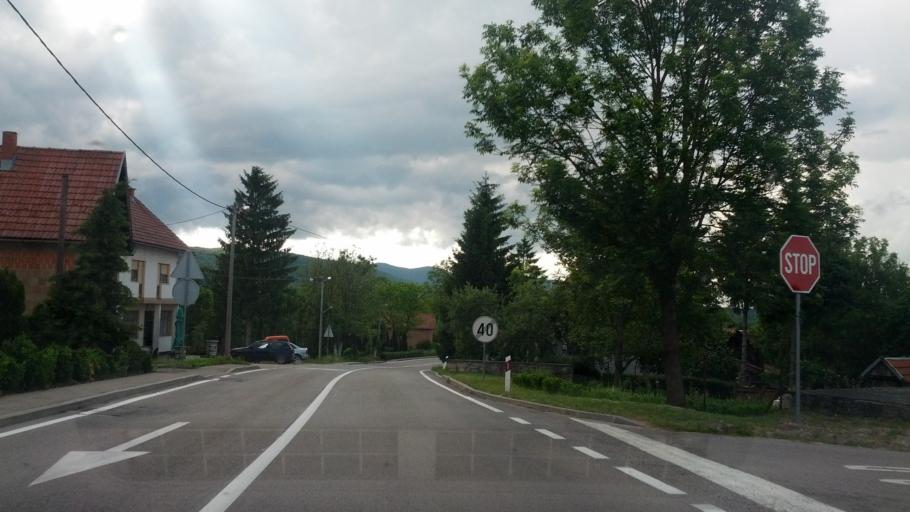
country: BA
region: Federation of Bosnia and Herzegovina
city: Izacic
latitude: 44.9067
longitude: 15.7208
